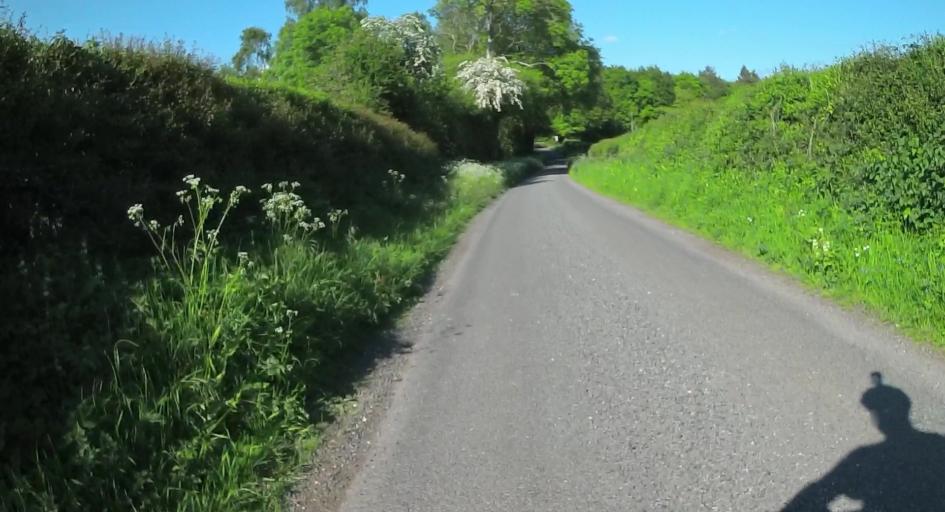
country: GB
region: England
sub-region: Hampshire
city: Overton
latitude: 51.1747
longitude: -1.2146
